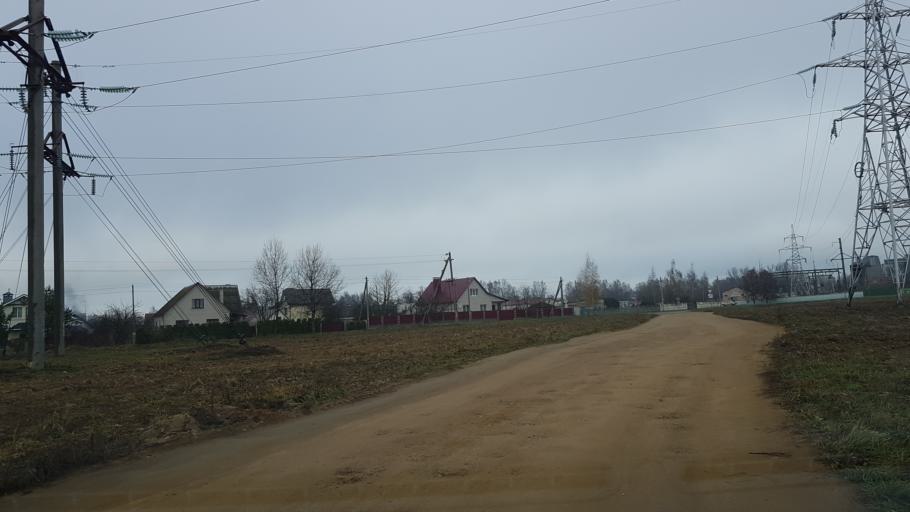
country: BY
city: Fanipol
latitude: 53.7343
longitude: 27.3241
